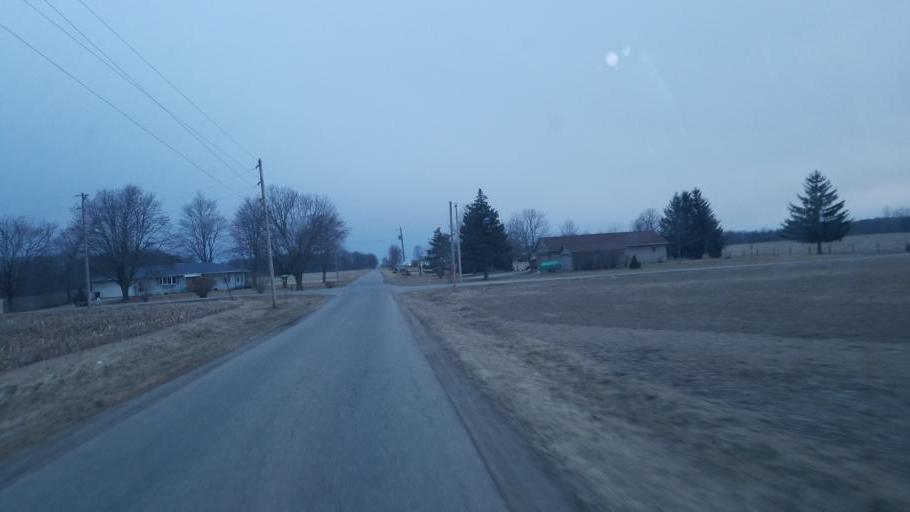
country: US
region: Ohio
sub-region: Defiance County
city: Hicksville
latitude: 41.3394
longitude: -84.7276
